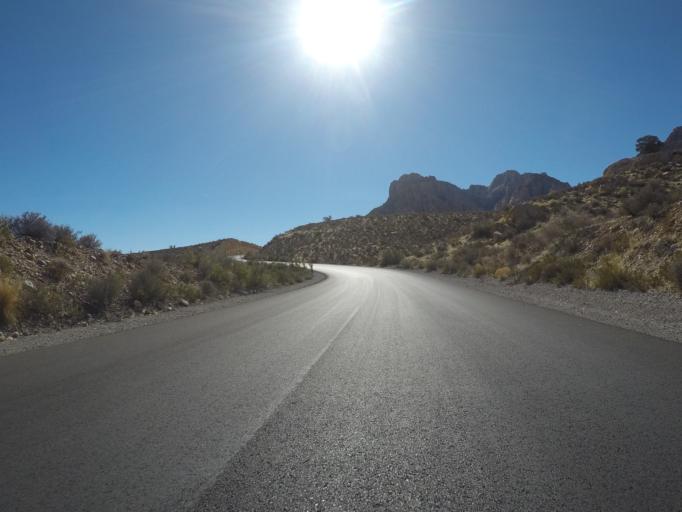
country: US
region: Nevada
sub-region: Clark County
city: Summerlin South
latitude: 36.1575
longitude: -115.4839
